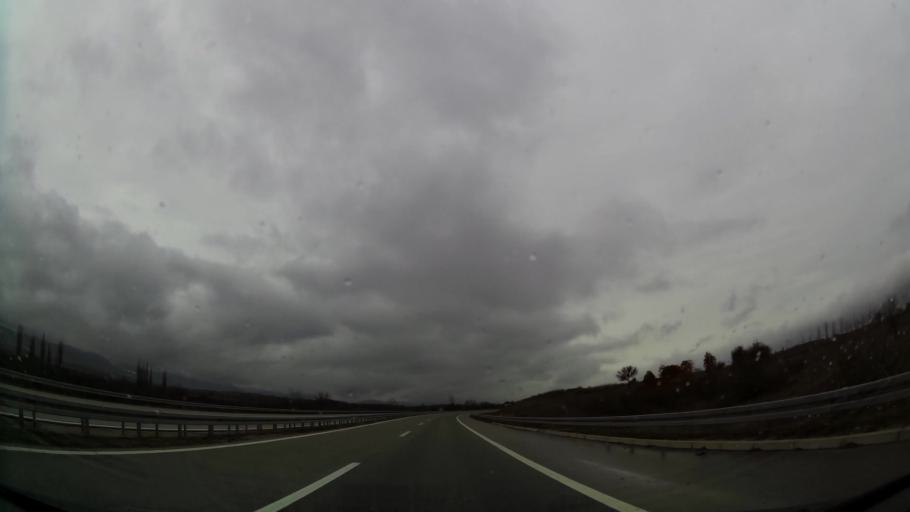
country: RS
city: Miratovac
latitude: 42.2607
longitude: 21.7009
